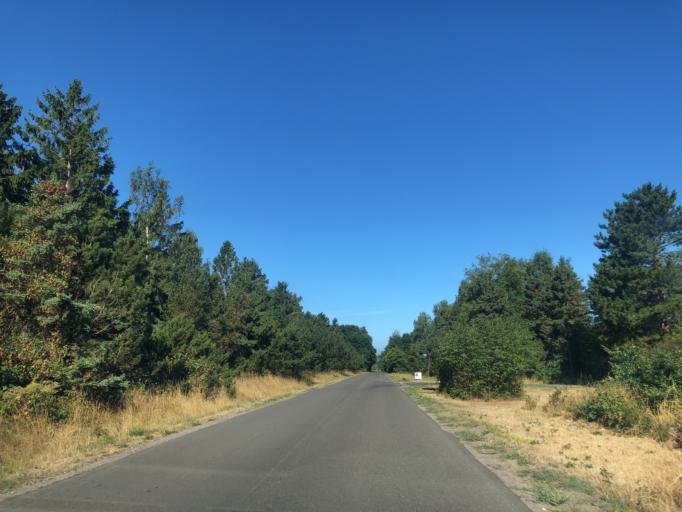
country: DK
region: Zealand
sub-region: Slagelse Kommune
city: Forlev
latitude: 55.3791
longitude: 11.2144
